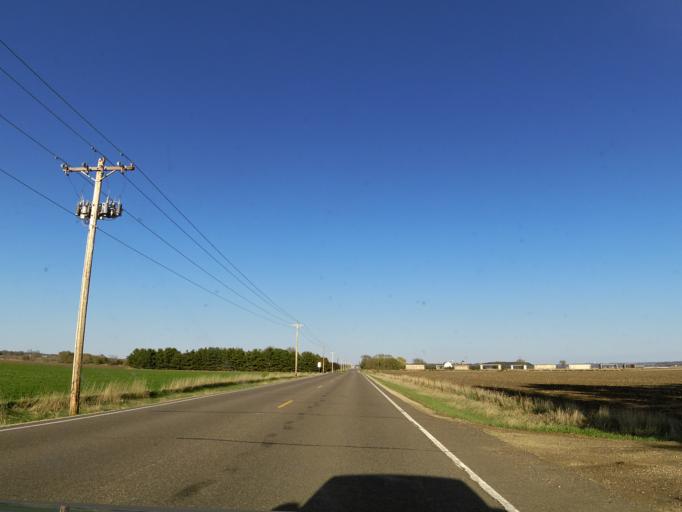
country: US
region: Minnesota
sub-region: Goodhue County
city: Cannon Falls
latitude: 44.5435
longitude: -93.0144
